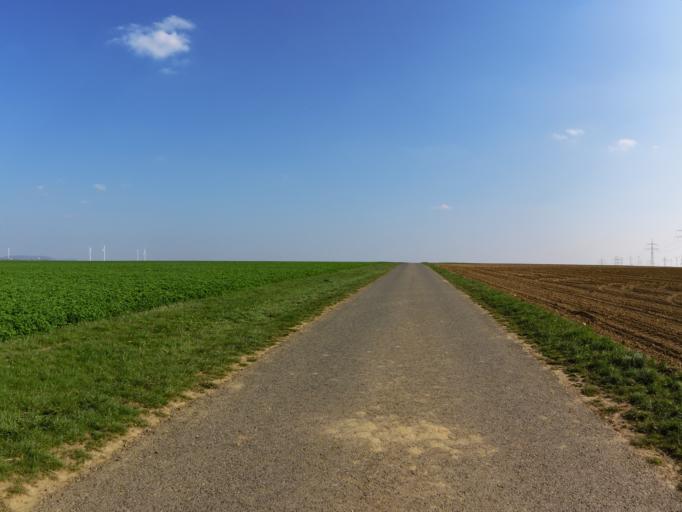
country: DE
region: Bavaria
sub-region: Regierungsbezirk Unterfranken
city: Biebelried
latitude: 49.7719
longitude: 10.0542
